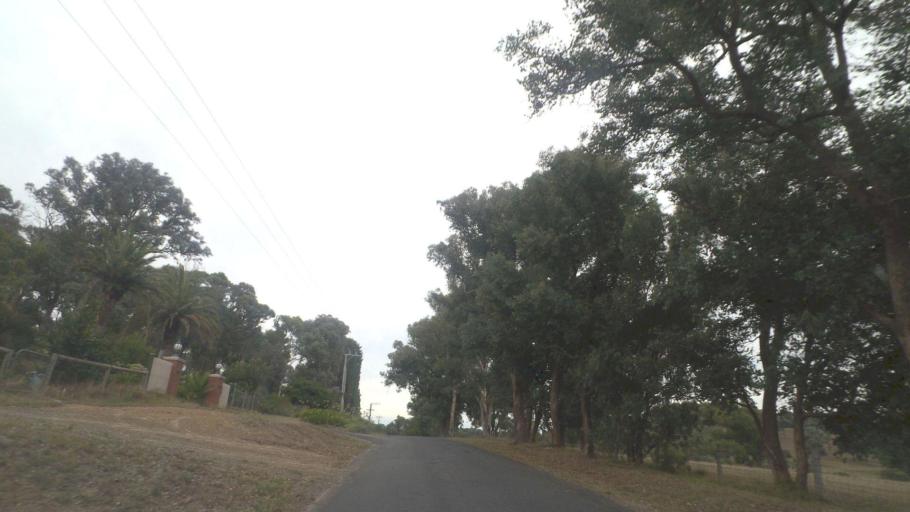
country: AU
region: Victoria
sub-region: Nillumbik
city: North Warrandyte
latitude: -37.7398
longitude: 145.1852
